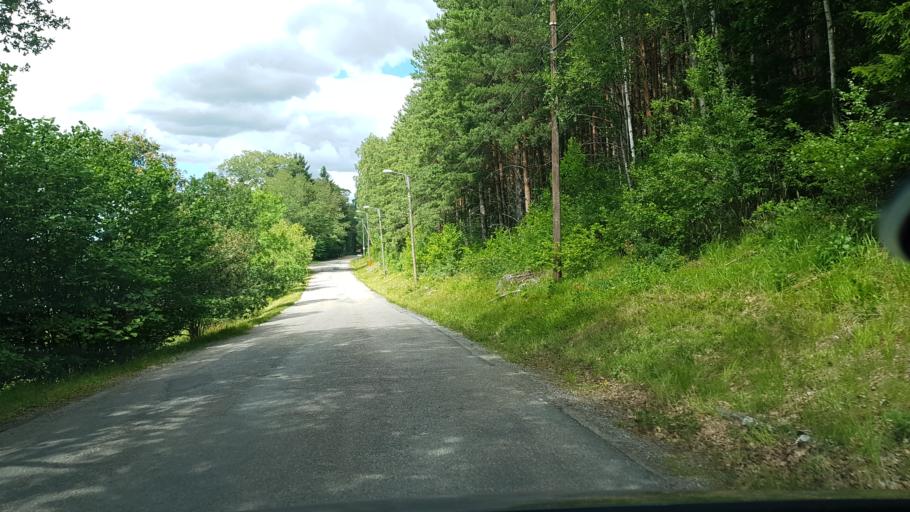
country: SE
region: Stockholm
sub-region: Upplands-Bro Kommun
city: Kungsaengen
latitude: 59.4896
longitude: 17.8043
